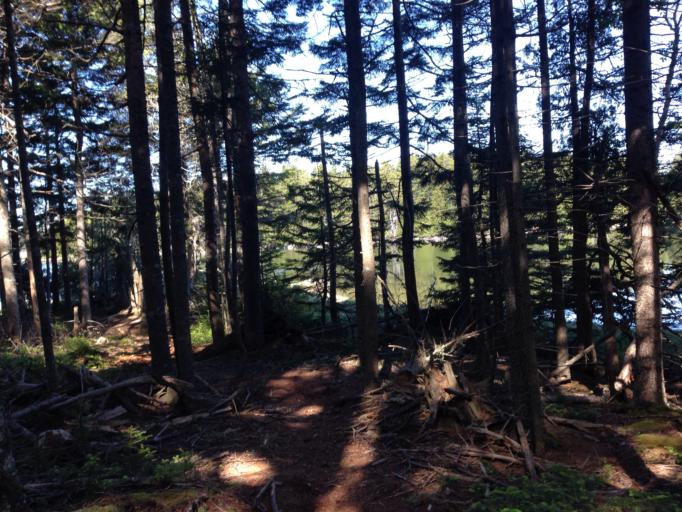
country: US
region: Maine
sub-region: Hancock County
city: Gouldsboro
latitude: 44.3844
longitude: -68.0722
